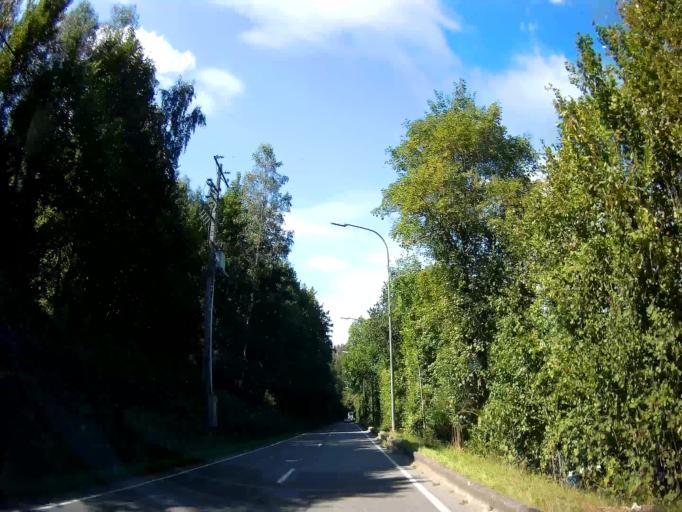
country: BE
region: Wallonia
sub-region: Province du Luxembourg
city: La Roche-en-Ardenne
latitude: 50.1852
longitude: 5.5474
